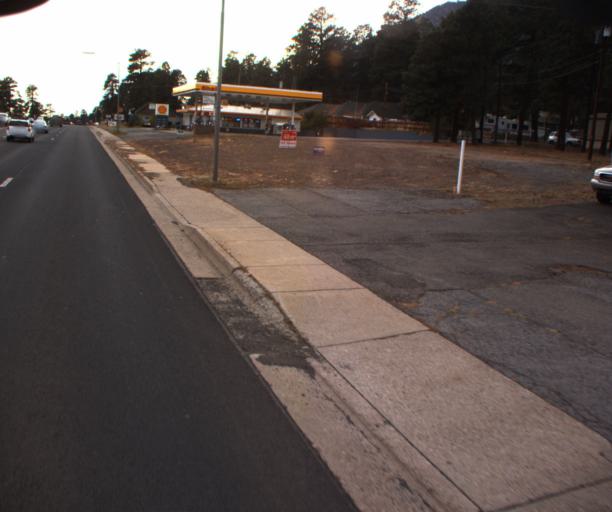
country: US
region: Arizona
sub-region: Coconino County
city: Flagstaff
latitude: 35.2426
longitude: -111.5678
